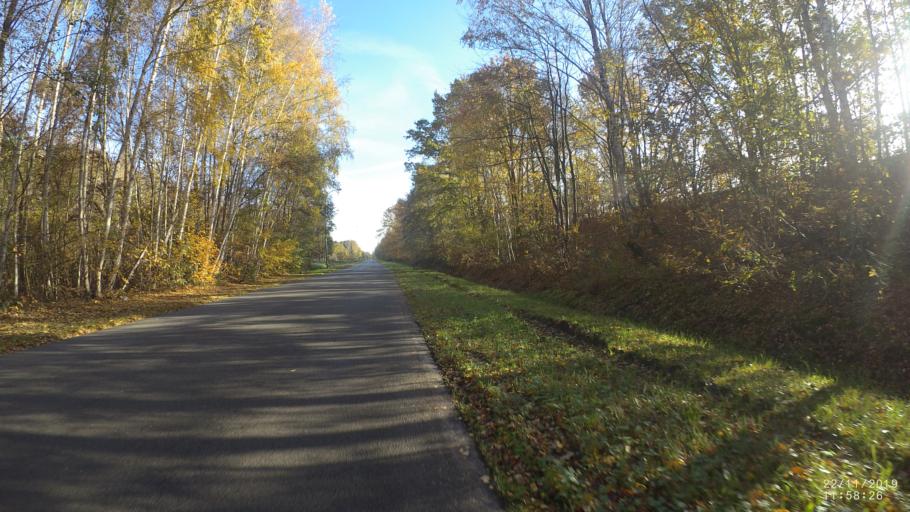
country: BE
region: Flanders
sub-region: Provincie Limburg
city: Hasselt
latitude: 50.9417
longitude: 5.3830
